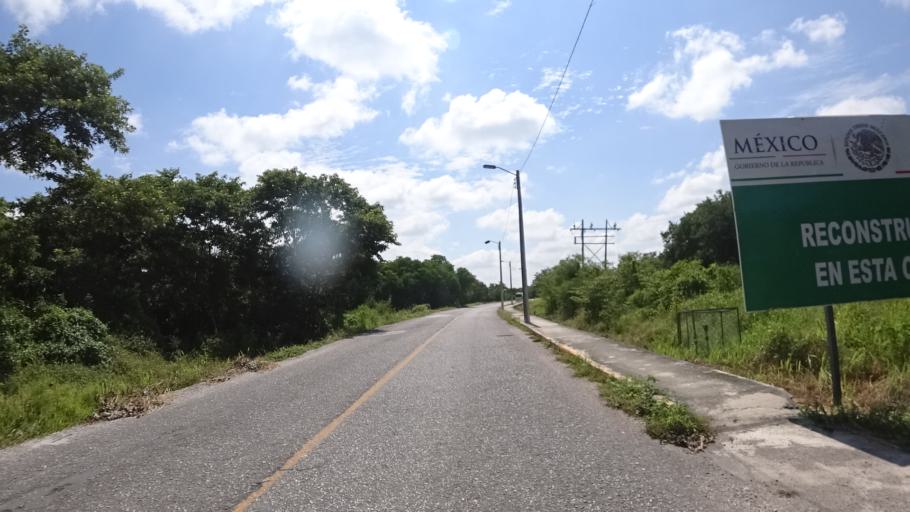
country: MX
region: Campeche
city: Sabancuy
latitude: 18.9873
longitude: -91.1880
